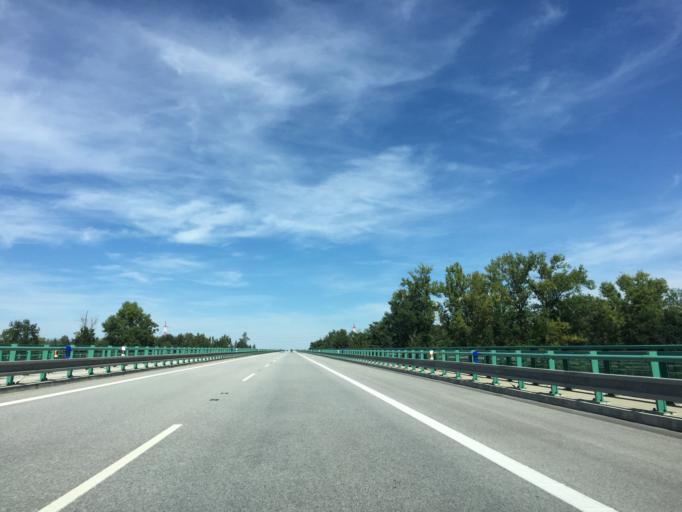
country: CZ
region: Jihocesky
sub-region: Okres Tabor
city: Veseli nad Luznici
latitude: 49.2081
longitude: 14.7121
